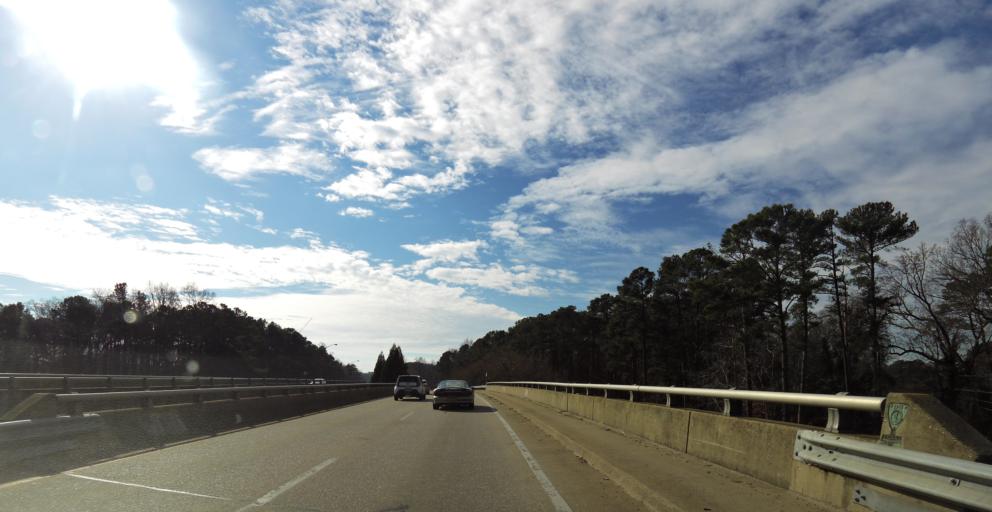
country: US
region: Virginia
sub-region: City of Newport News
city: Newport News
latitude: 37.0708
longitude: -76.4809
